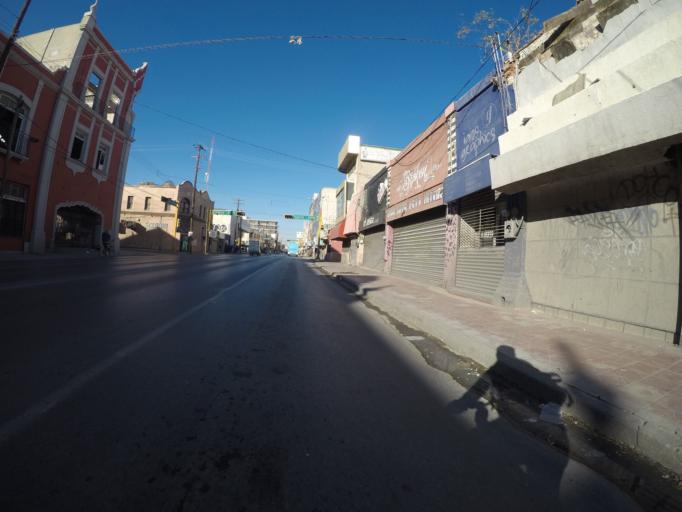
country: MX
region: Chihuahua
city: Ciudad Juarez
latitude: 31.7390
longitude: -106.4793
